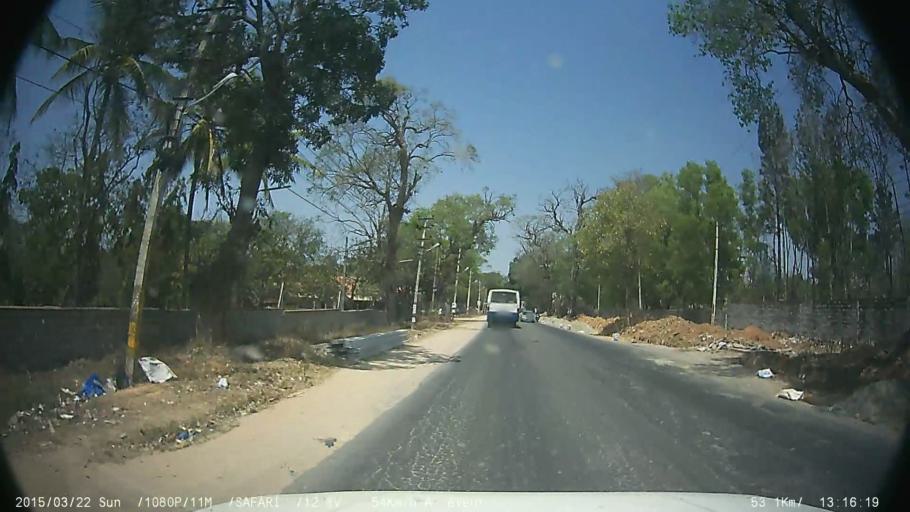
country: IN
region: Karnataka
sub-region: Bangalore Urban
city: Bangalore
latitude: 12.8298
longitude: 77.5877
